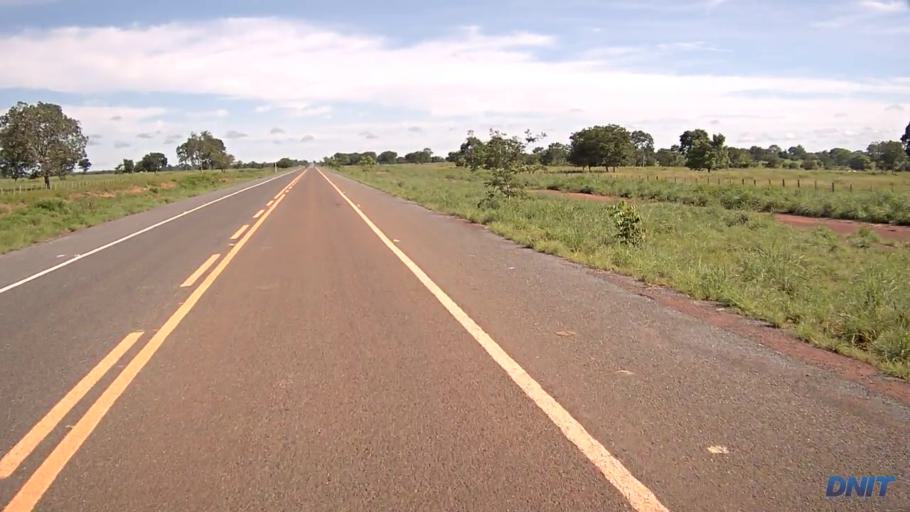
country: BR
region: Goias
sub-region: Sao Miguel Do Araguaia
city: Sao Miguel do Araguaia
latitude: -13.4684
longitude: -50.1155
